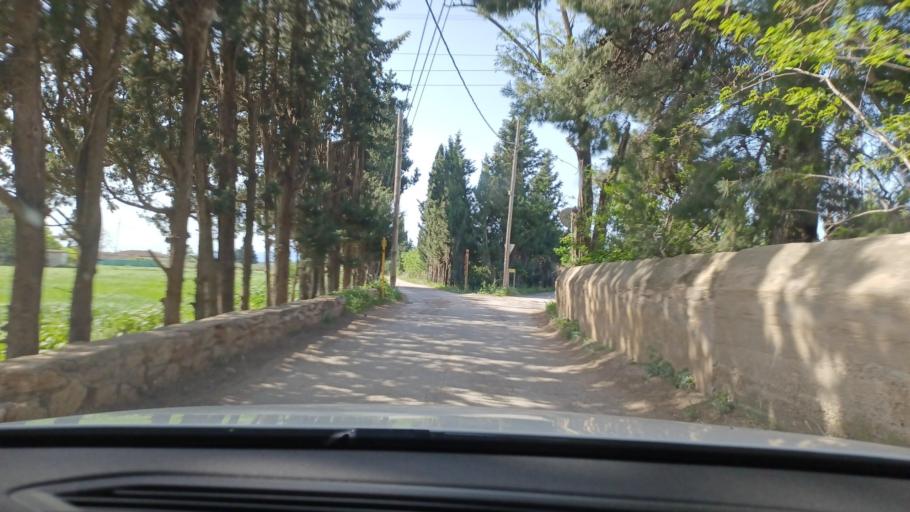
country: ES
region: Catalonia
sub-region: Provincia de Tarragona
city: Tortosa
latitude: 40.7975
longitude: 0.5171
